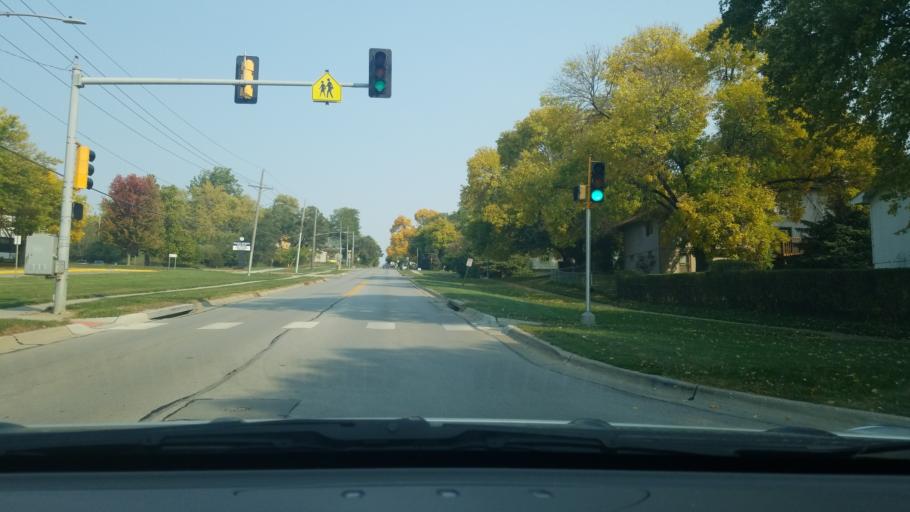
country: US
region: Nebraska
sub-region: Sarpy County
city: Bellevue
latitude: 41.1536
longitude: -95.9090
